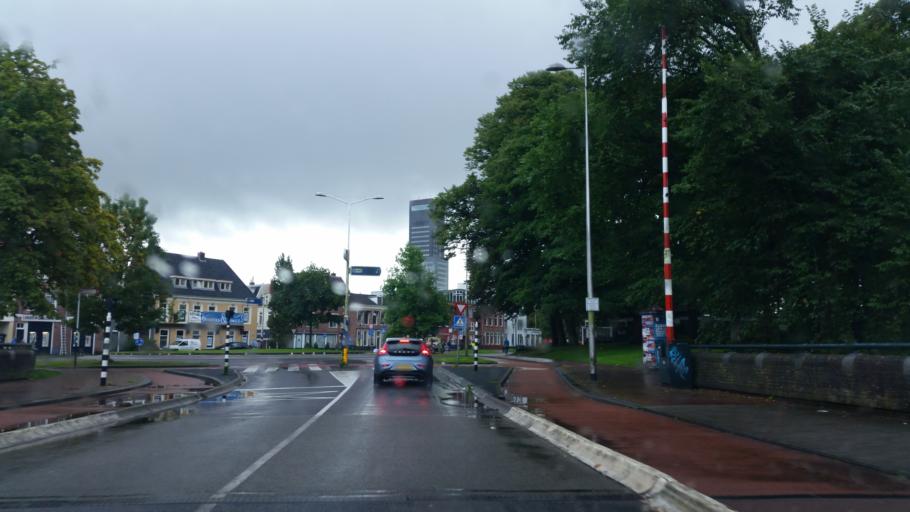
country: NL
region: Friesland
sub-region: Gemeente Leeuwarden
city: Bilgaard
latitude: 53.2026
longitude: 5.7882
